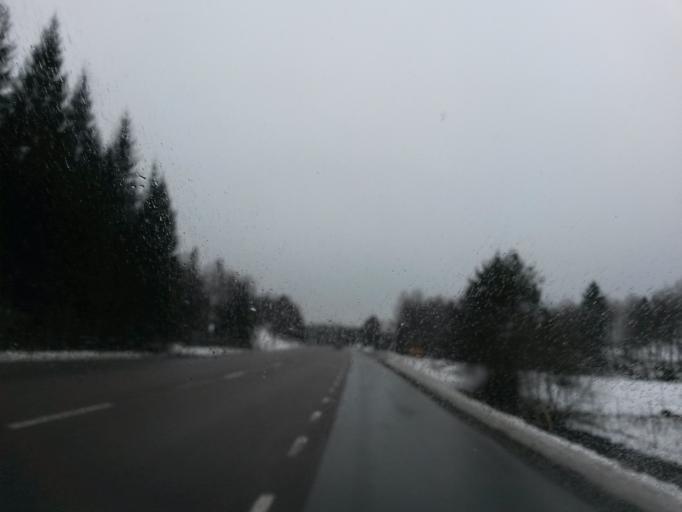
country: SE
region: Vaestra Goetaland
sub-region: Boras Kommun
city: Viskafors
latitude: 57.6421
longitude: 12.9068
